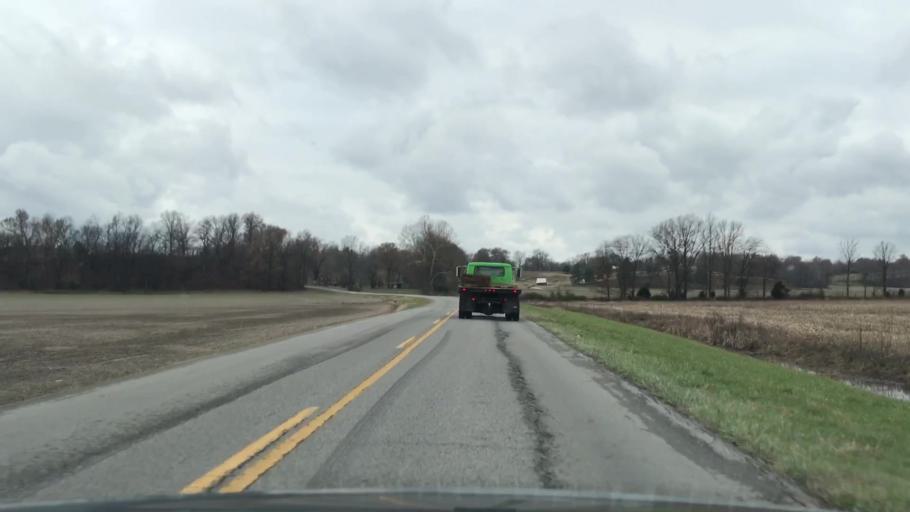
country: US
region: Kentucky
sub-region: McLean County
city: Calhoun
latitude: 37.5225
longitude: -87.3827
